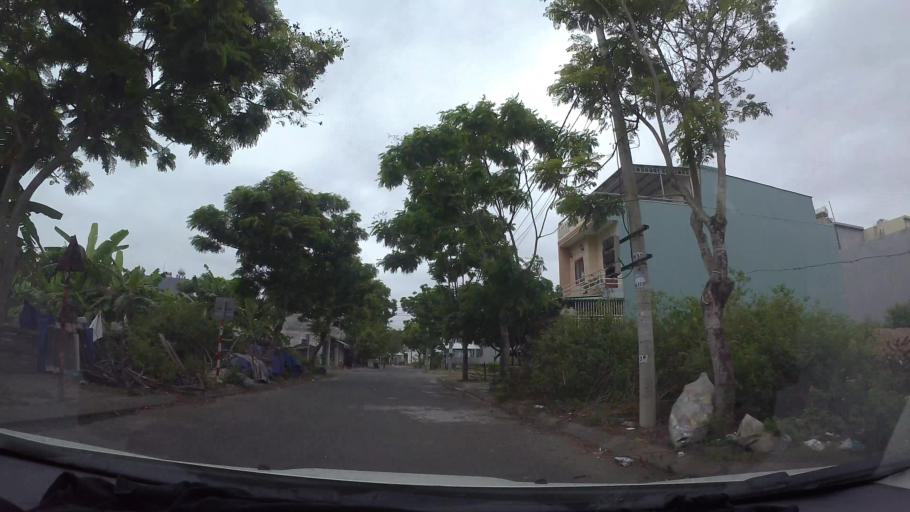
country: VN
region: Da Nang
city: Lien Chieu
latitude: 16.1252
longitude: 108.1185
